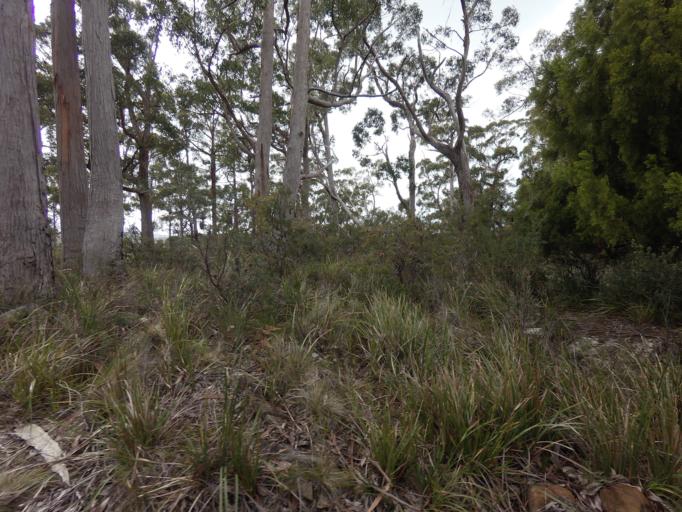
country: AU
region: Tasmania
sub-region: Huon Valley
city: Geeveston
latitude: -43.4683
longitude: 146.9316
